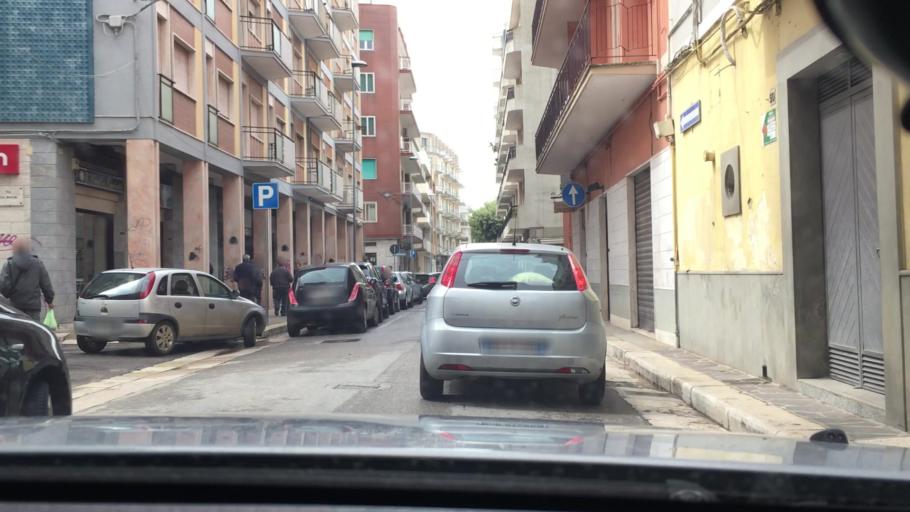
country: IT
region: Apulia
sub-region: Provincia di Bari
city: Gioia del Colle
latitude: 40.7969
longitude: 16.9201
